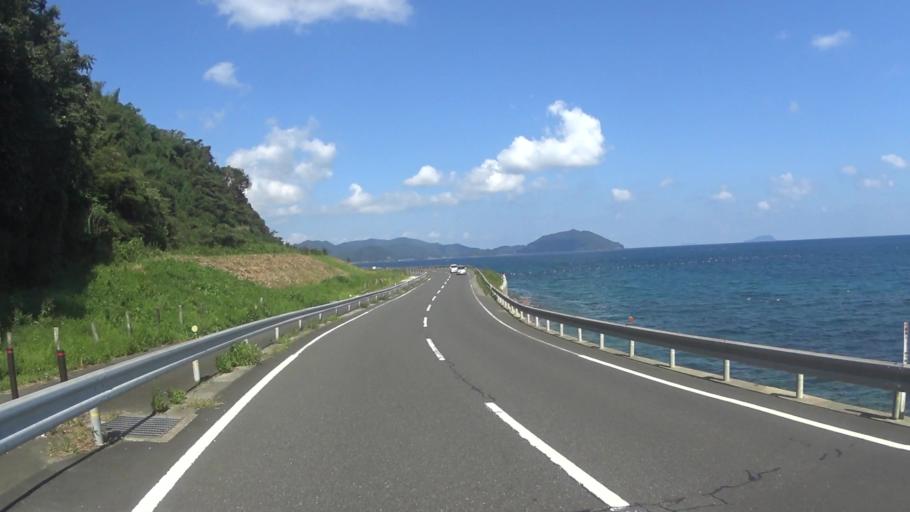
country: JP
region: Kyoto
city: Miyazu
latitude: 35.6310
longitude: 135.2458
